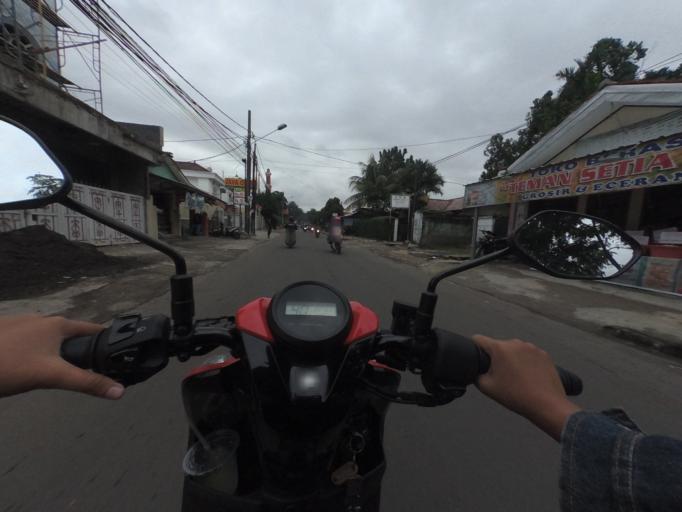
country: ID
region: West Java
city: Bogor
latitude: -6.5670
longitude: 106.8008
